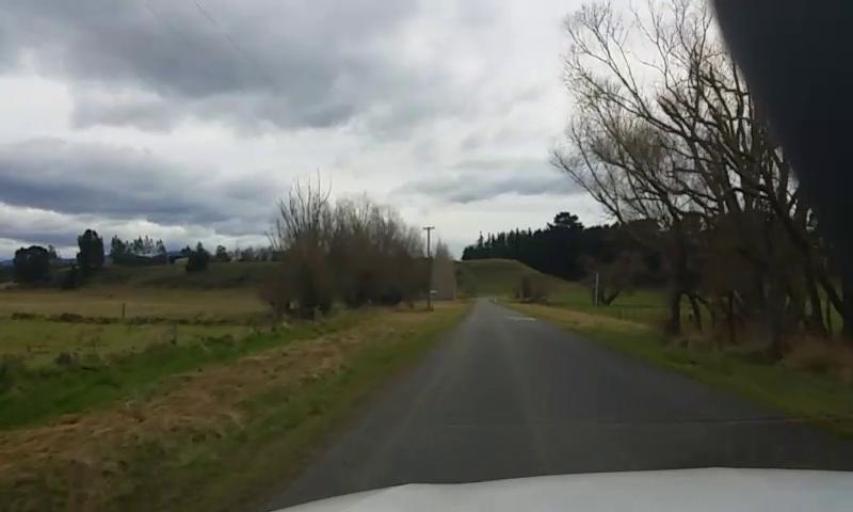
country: NZ
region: Canterbury
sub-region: Waimakariri District
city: Kaiapoi
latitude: -43.3013
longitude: 172.4379
